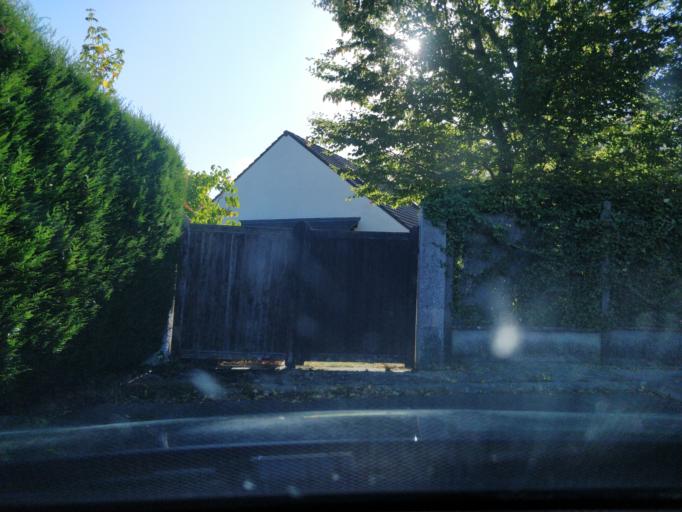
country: FR
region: Ile-de-France
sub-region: Departement de l'Essonne
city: Forges-les-Bains
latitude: 48.6281
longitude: 2.0909
